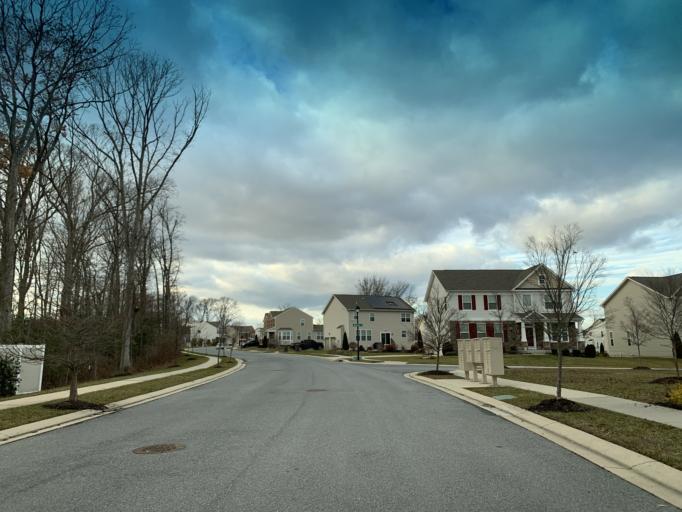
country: US
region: Maryland
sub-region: Baltimore County
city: Middle River
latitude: 39.3442
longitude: -76.4331
